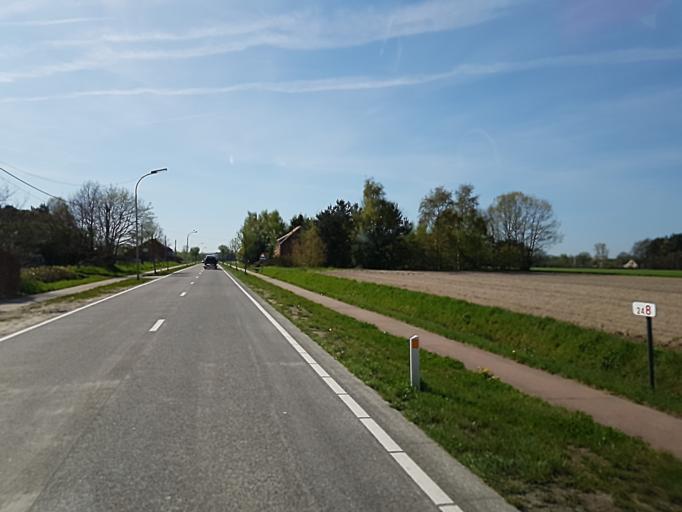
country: BE
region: Flanders
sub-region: Provincie Antwerpen
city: Westerlo
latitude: 51.1120
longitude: 4.9436
